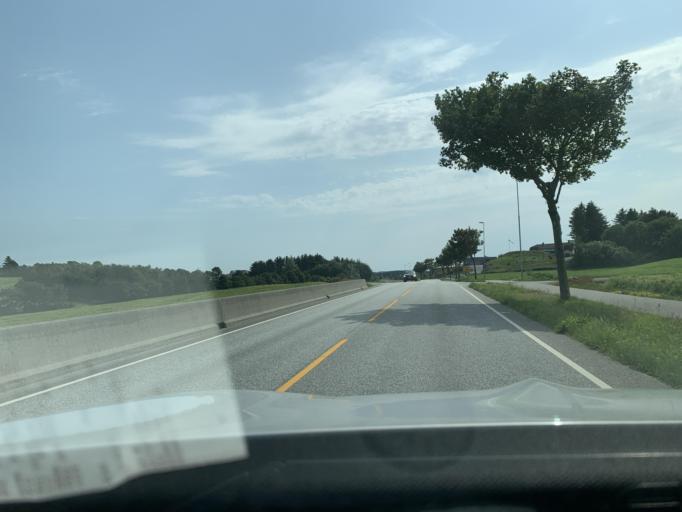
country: NO
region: Rogaland
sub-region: Klepp
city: Kleppe
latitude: 58.7635
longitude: 5.6251
